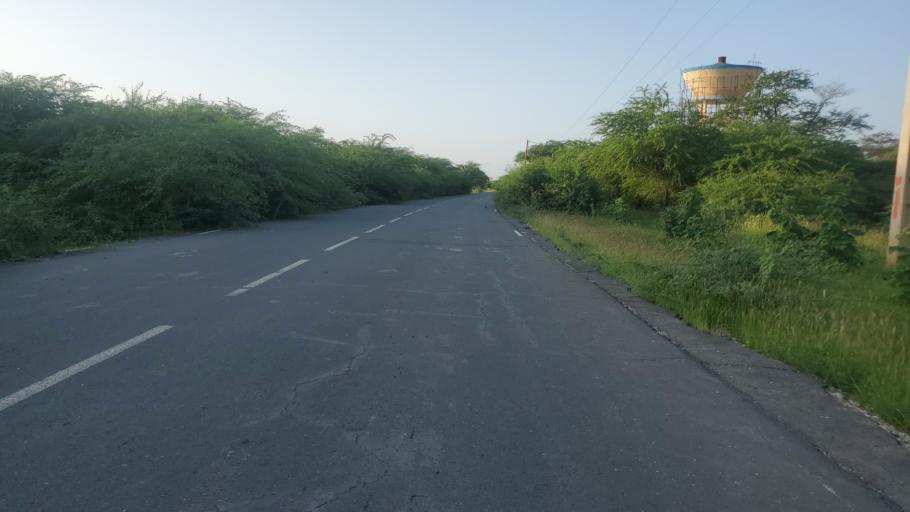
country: SN
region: Saint-Louis
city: Saint-Louis
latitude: 16.2067
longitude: -16.4152
